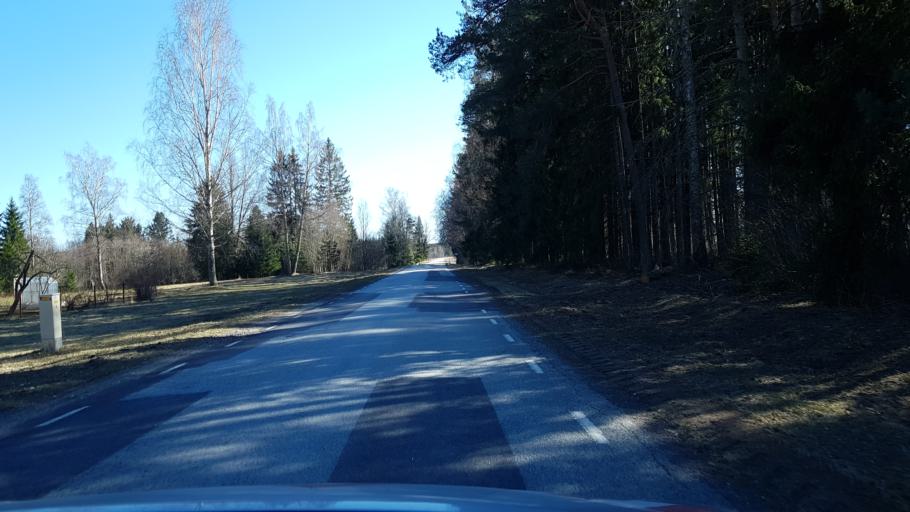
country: EE
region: Laeaene-Virumaa
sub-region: Viru-Nigula vald
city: Kunda
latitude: 59.3817
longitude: 26.5754
